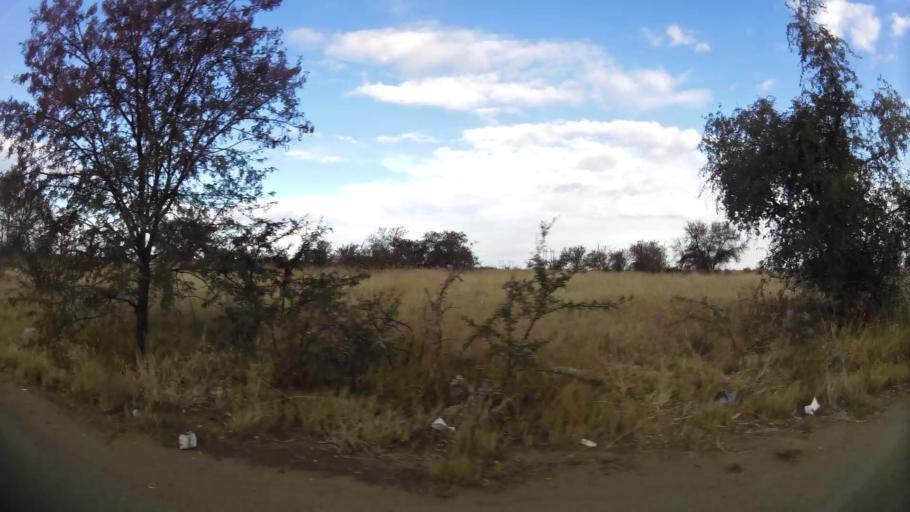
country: ZA
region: Orange Free State
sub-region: Lejweleputswa District Municipality
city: Welkom
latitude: -28.0037
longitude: 26.7343
